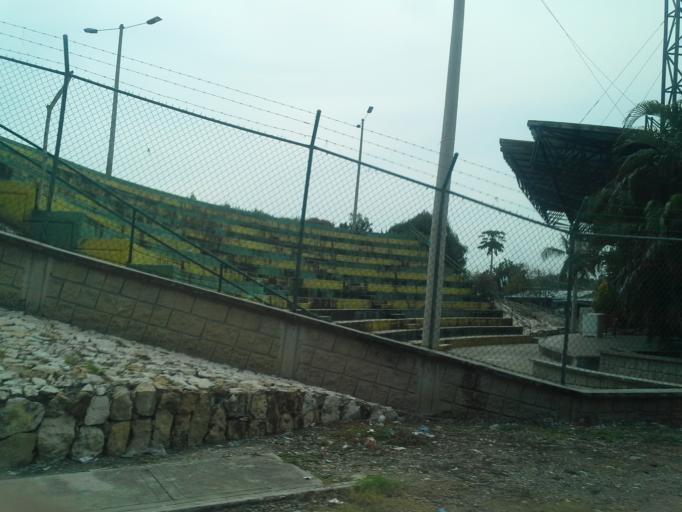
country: CO
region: Sucre
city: Ovejas
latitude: 9.5294
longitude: -75.2272
